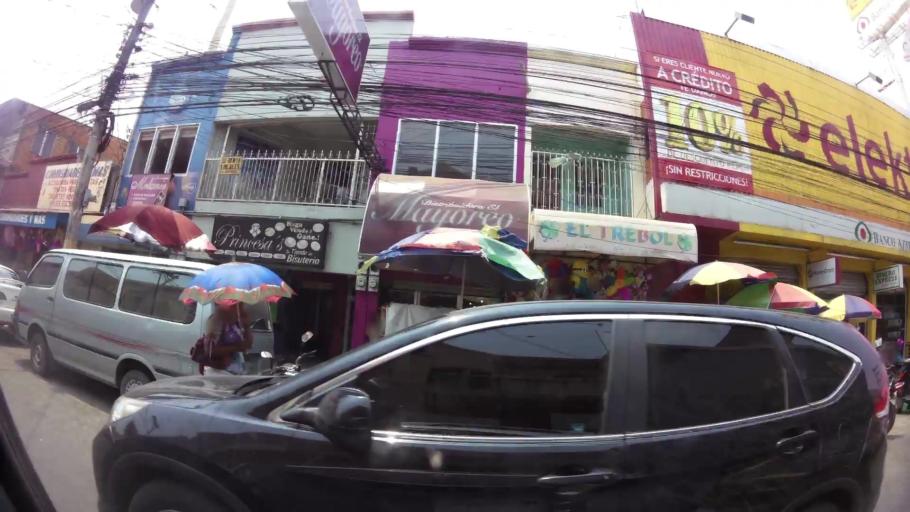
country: HN
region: Yoro
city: El Progreso
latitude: 15.4015
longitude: -87.8090
